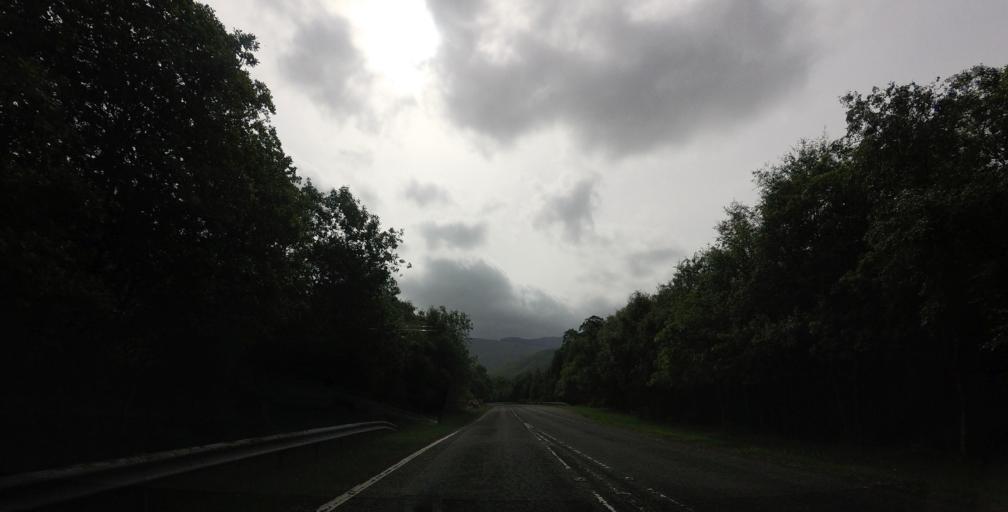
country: GB
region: Scotland
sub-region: Argyll and Bute
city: Isle Of Mull
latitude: 56.8793
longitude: -5.6759
